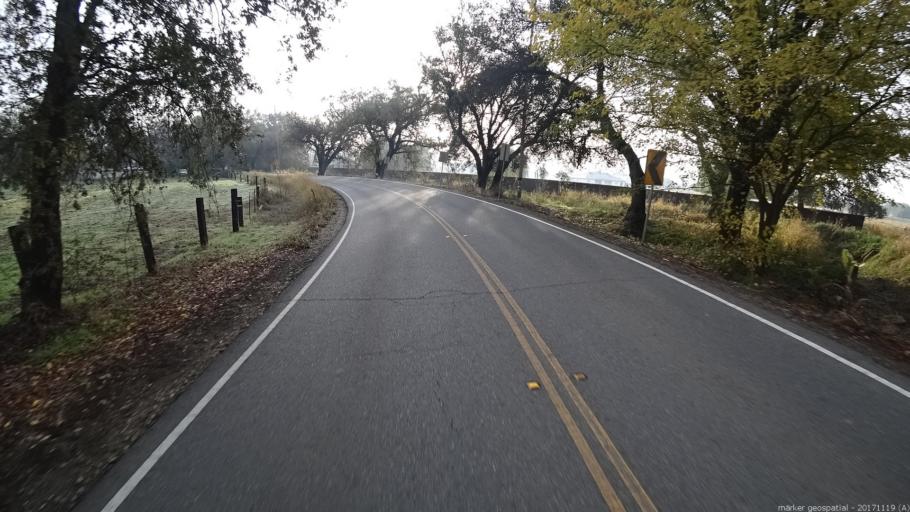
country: US
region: California
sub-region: Shasta County
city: Anderson
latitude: 40.4985
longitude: -122.3236
